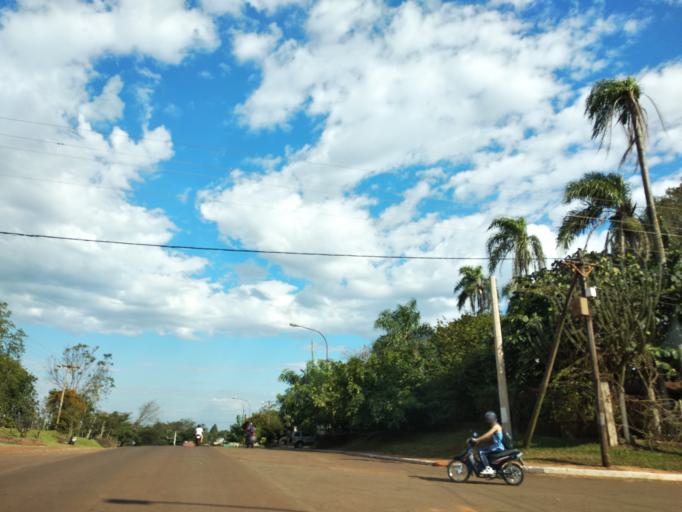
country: AR
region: Misiones
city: Aristobulo del Valle
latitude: -27.0835
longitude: -54.8310
